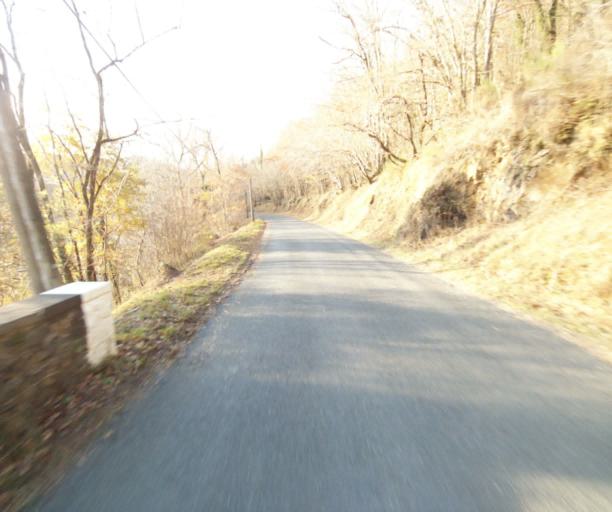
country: FR
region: Limousin
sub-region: Departement de la Correze
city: Laguenne
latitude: 45.2402
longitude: 1.7973
